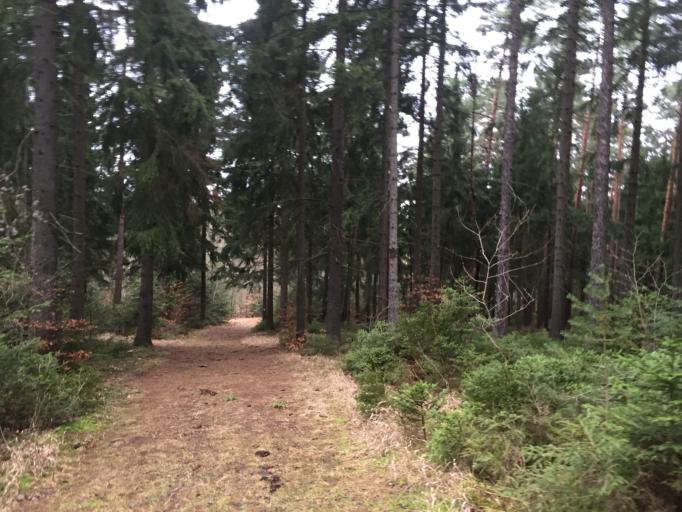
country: DE
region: Thuringia
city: Bad Blankenburg
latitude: 50.7102
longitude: 11.2252
